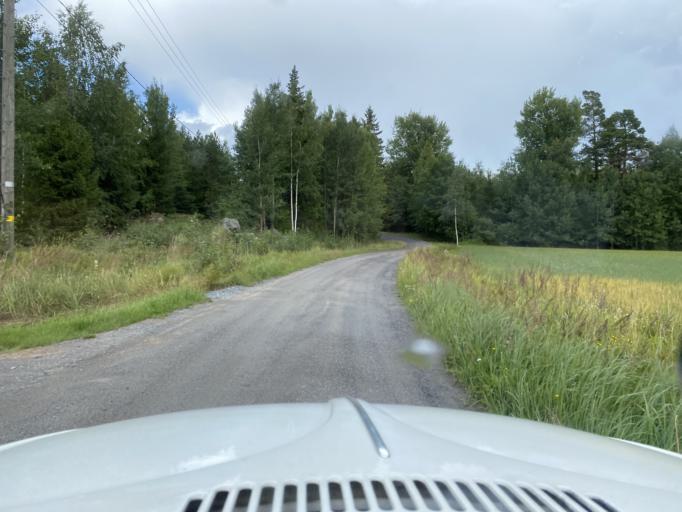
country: FI
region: Pirkanmaa
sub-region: Lounais-Pirkanmaa
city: Punkalaidun
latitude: 61.1266
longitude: 23.0638
